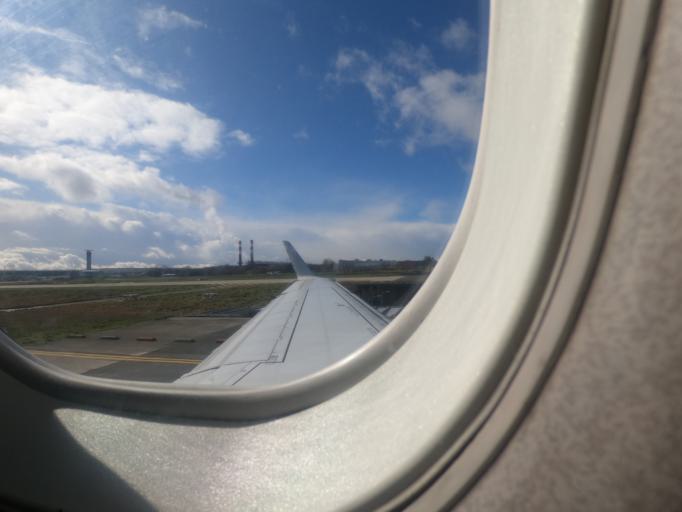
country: FR
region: Ile-de-France
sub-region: Departement de Seine-et-Marne
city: Mitry-Mory
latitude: 49.0122
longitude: 2.5818
